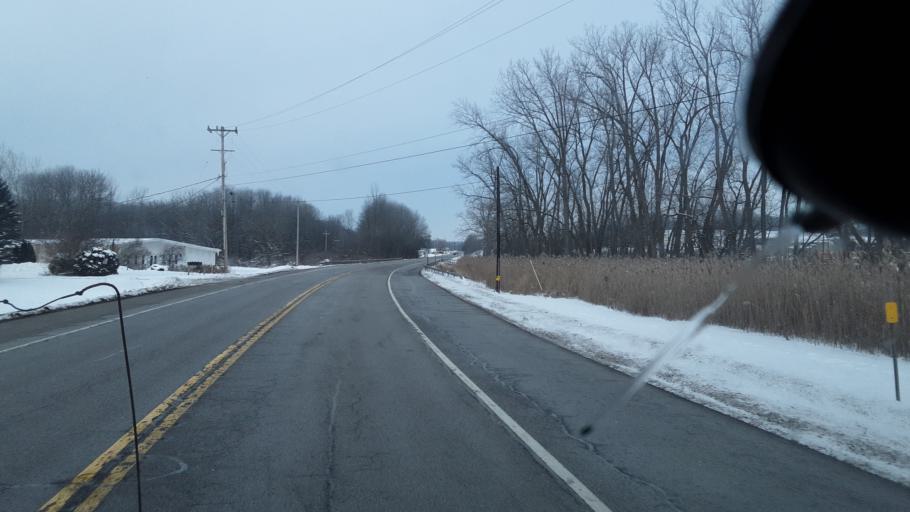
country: US
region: New York
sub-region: Wayne County
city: Lyons
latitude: 43.0596
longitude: -77.0144
